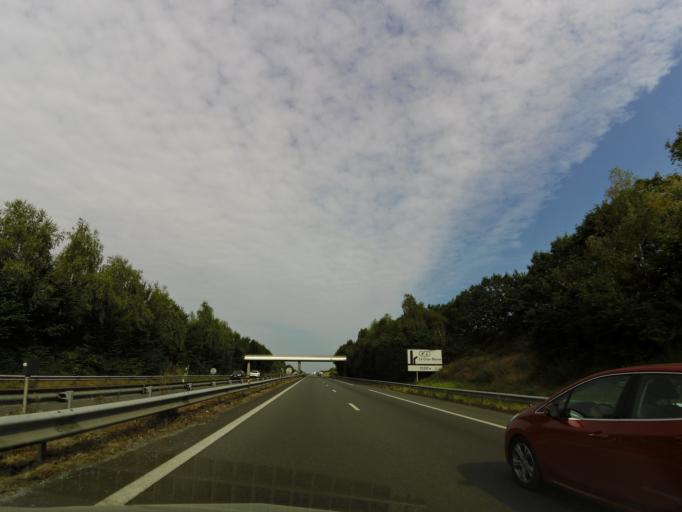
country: FR
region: Pays de la Loire
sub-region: Departement de la Loire-Atlantique
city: Le Bignon
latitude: 47.1179
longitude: -1.4948
